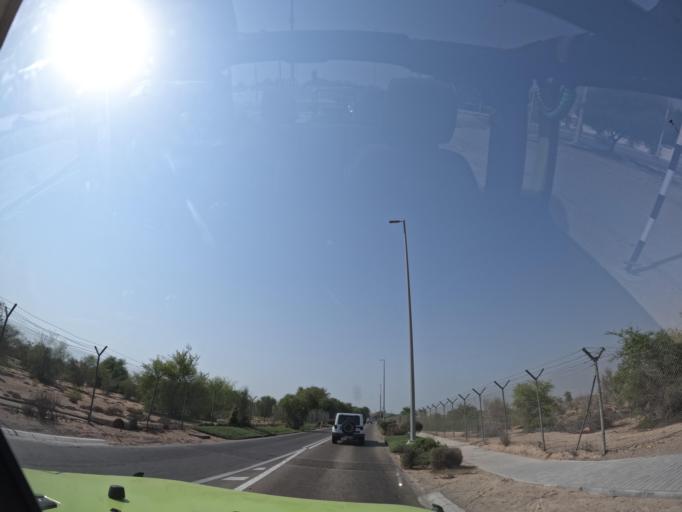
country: AE
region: Abu Dhabi
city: Abu Dhabi
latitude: 24.4729
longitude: 54.6302
